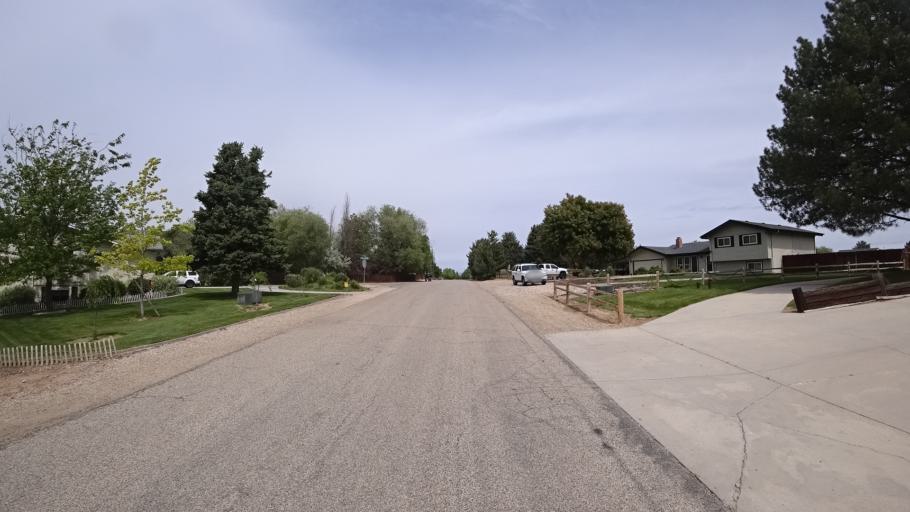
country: US
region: Idaho
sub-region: Ada County
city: Meridian
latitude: 43.5549
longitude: -116.3243
